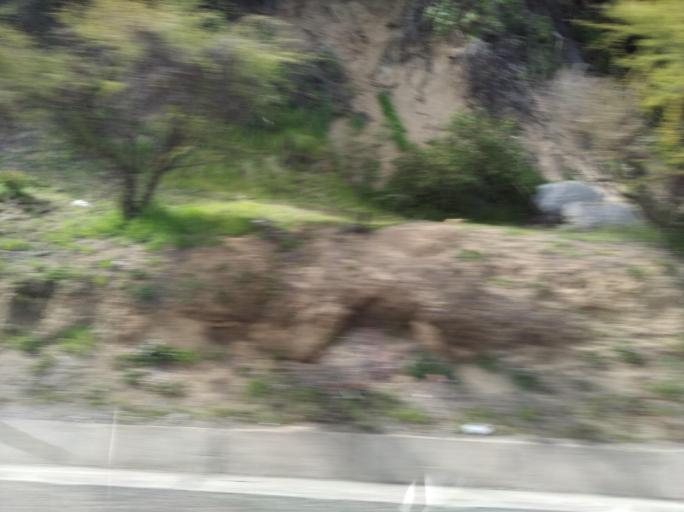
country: CL
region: Valparaiso
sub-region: Provincia de San Felipe
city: Llaillay
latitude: -33.0619
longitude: -71.0155
